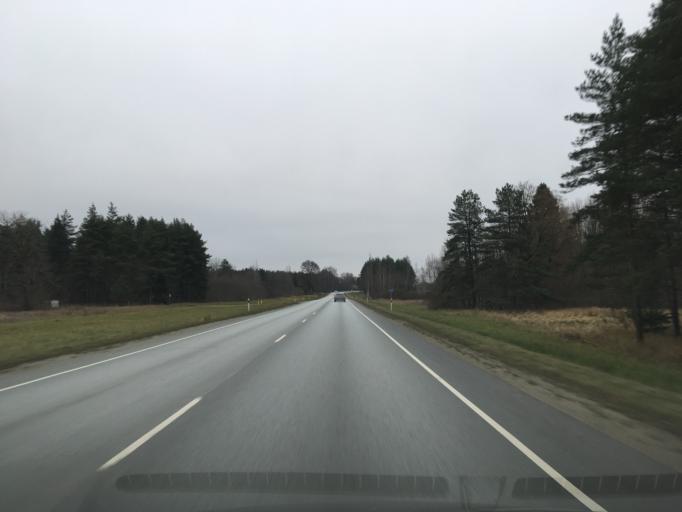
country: EE
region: Laeaene-Virumaa
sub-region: Viru-Nigula vald
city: Kunda
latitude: 59.4036
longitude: 26.6339
